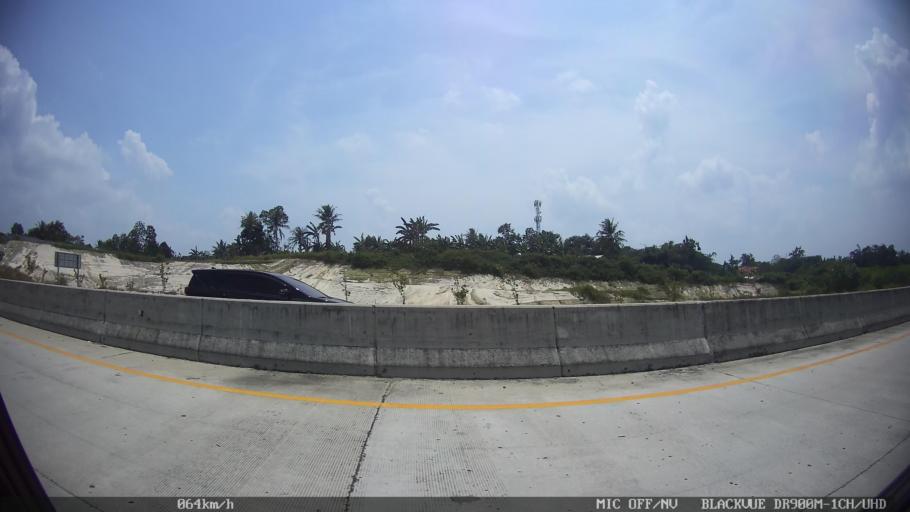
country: ID
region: Lampung
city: Natar
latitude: -5.2898
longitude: 105.2261
